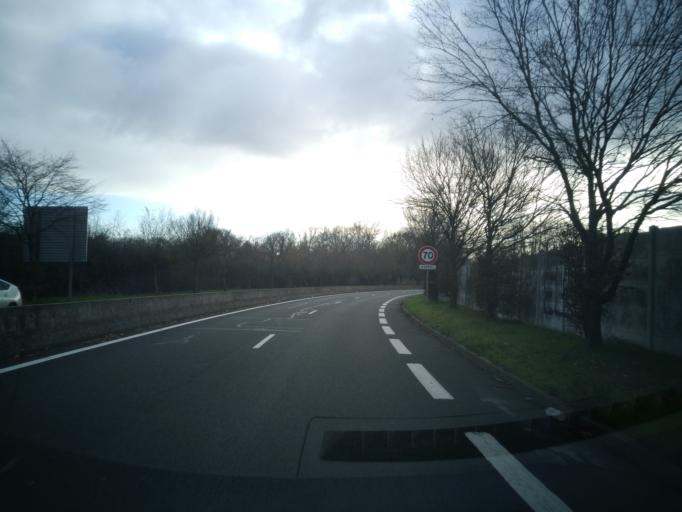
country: FR
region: Ile-de-France
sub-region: Departement des Yvelines
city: Buc
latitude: 48.7832
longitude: 2.1064
